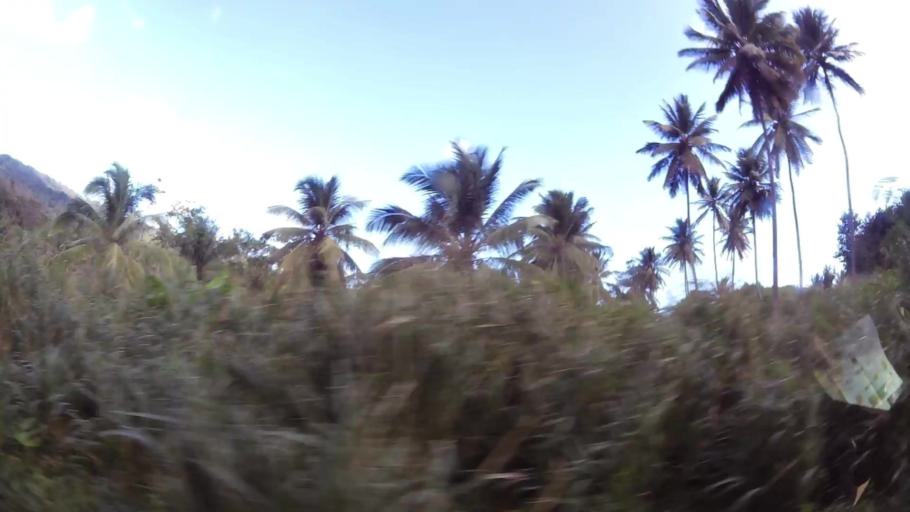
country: DM
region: Saint Andrew
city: Marigot
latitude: 15.5170
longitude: -61.2746
